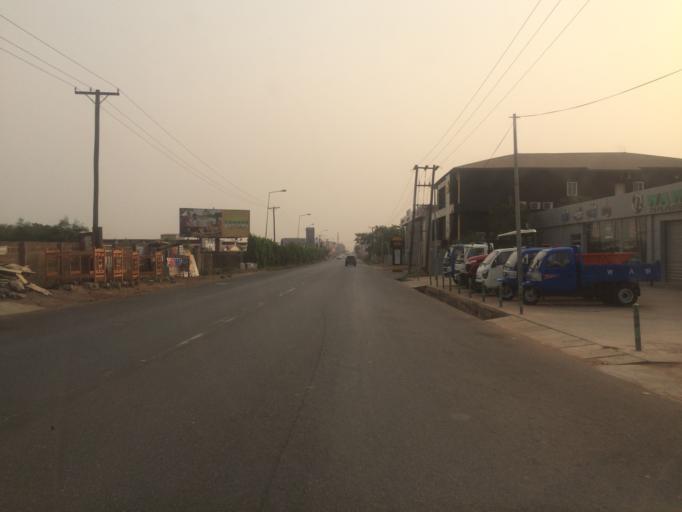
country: GH
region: Greater Accra
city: Medina Estates
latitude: 5.6394
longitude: -0.1220
